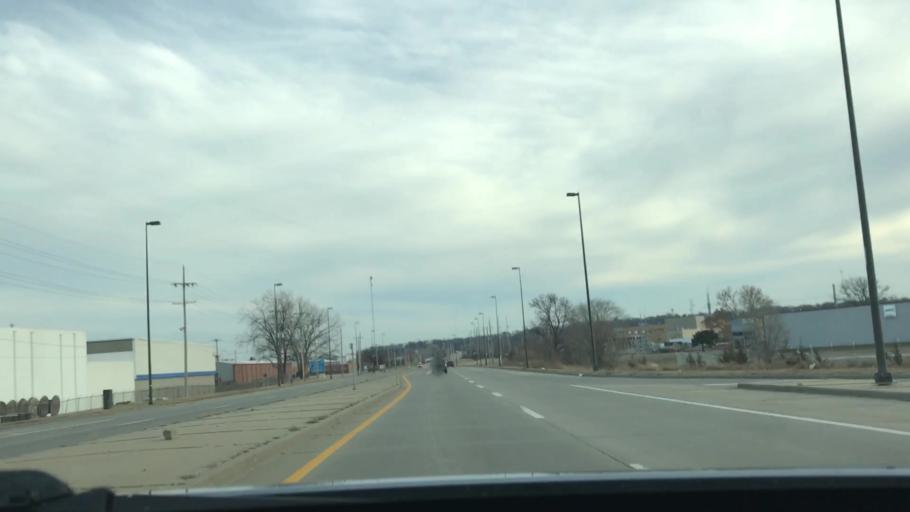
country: US
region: Missouri
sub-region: Clay County
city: North Kansas City
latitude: 39.1376
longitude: -94.5290
